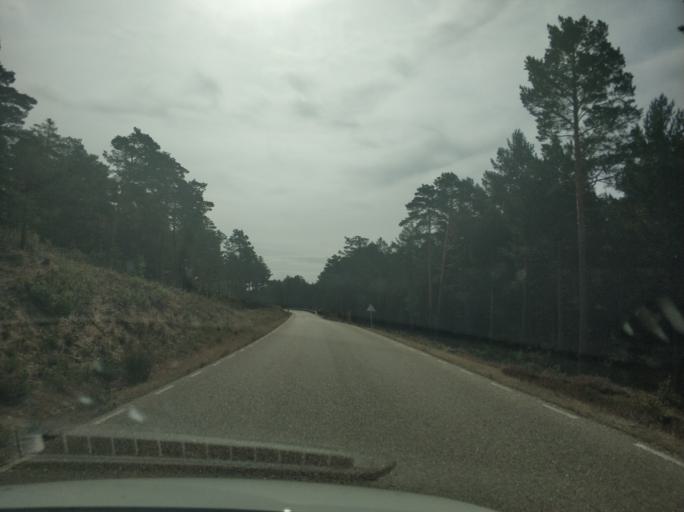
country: ES
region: Castille and Leon
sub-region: Provincia de Soria
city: Navaleno
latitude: 41.8555
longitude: -2.9667
